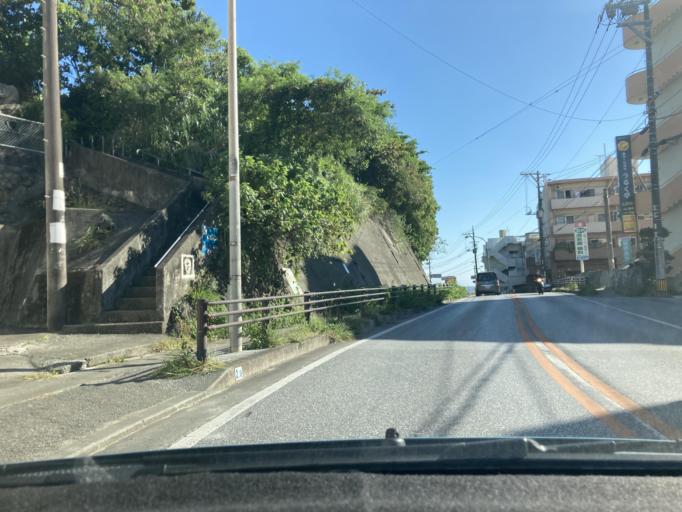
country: JP
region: Okinawa
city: Tomigusuku
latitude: 26.1828
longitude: 127.6622
